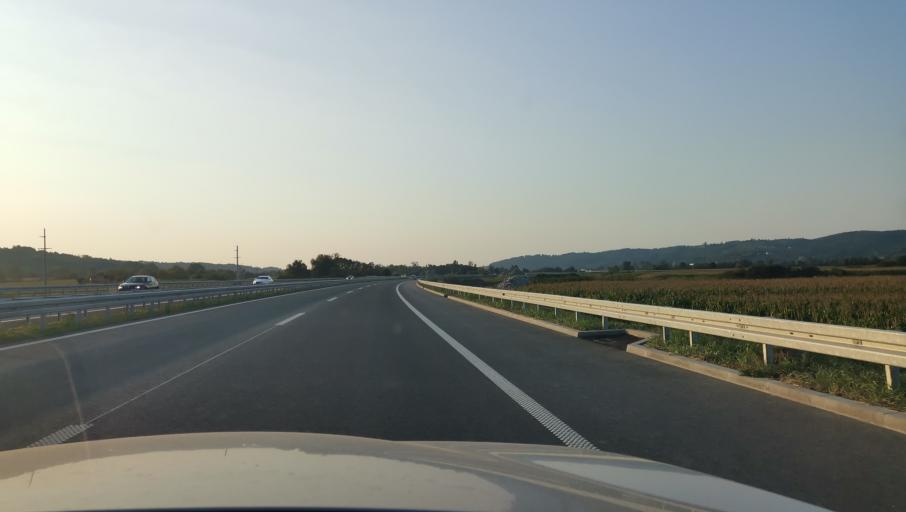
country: RS
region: Central Serbia
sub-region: Kolubarski Okrug
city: Lajkovac
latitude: 44.3143
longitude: 20.2164
